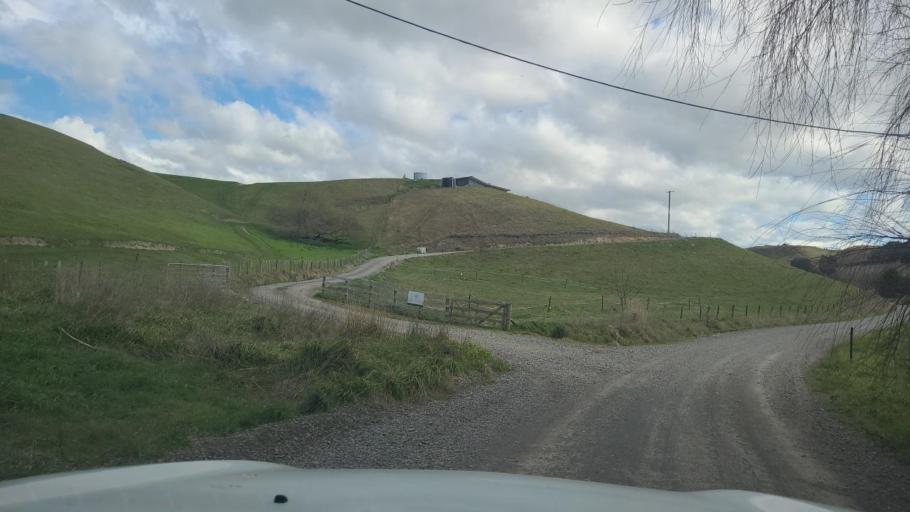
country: NZ
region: Hawke's Bay
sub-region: Hastings District
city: Hastings
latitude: -39.6621
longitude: 176.6571
